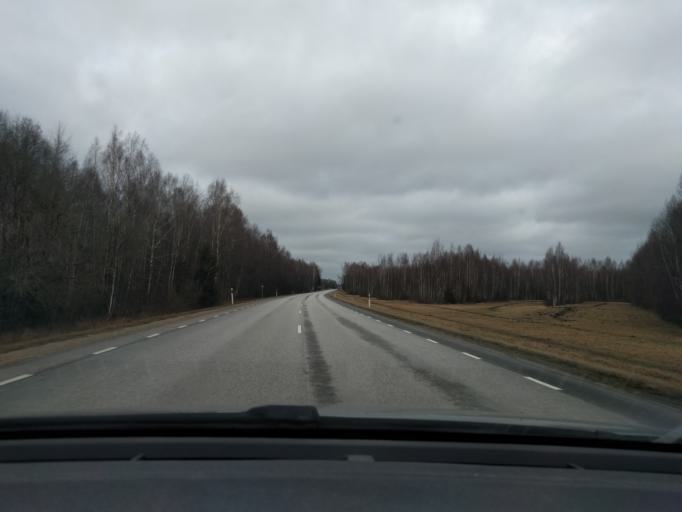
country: EE
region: Viljandimaa
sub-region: Vohma linn
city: Vohma
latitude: 58.5783
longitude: 25.5693
